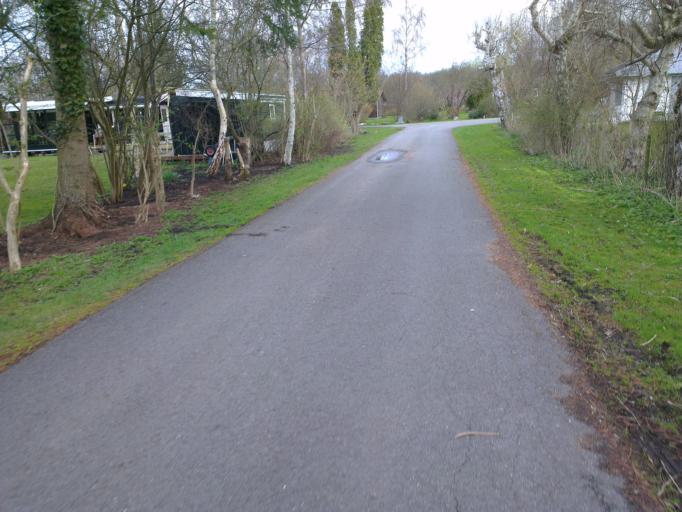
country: DK
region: Capital Region
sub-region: Frederikssund Kommune
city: Jaegerspris
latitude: 55.8411
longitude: 11.9658
